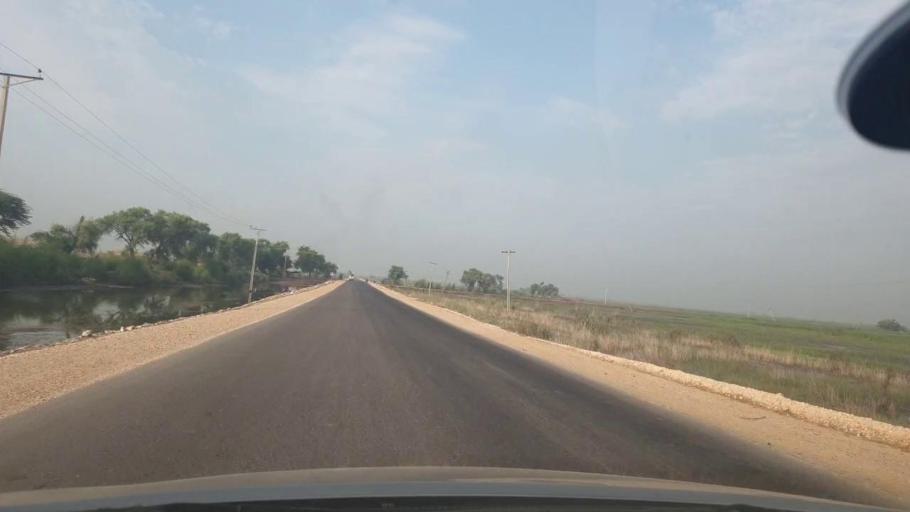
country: PK
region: Sindh
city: Jacobabad
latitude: 28.2346
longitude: 68.3879
